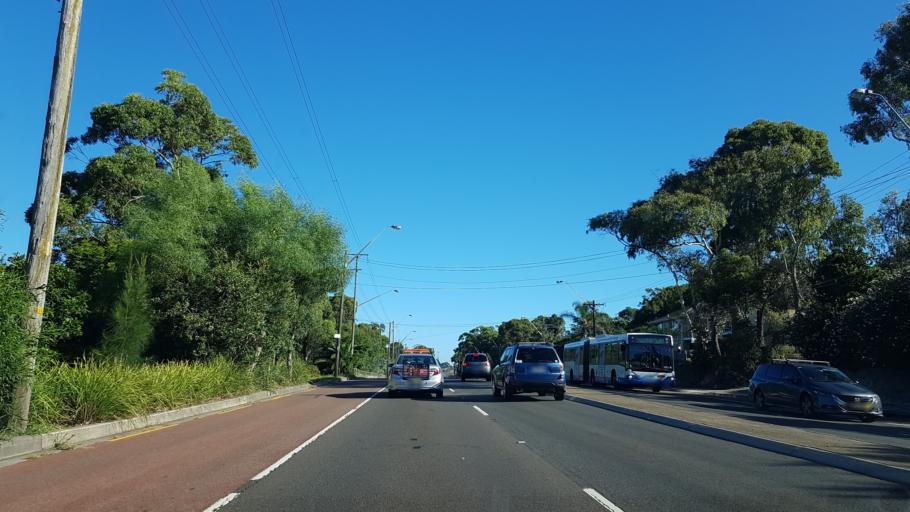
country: AU
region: New South Wales
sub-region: Pittwater
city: Warriewood
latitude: -33.6785
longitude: 151.3033
